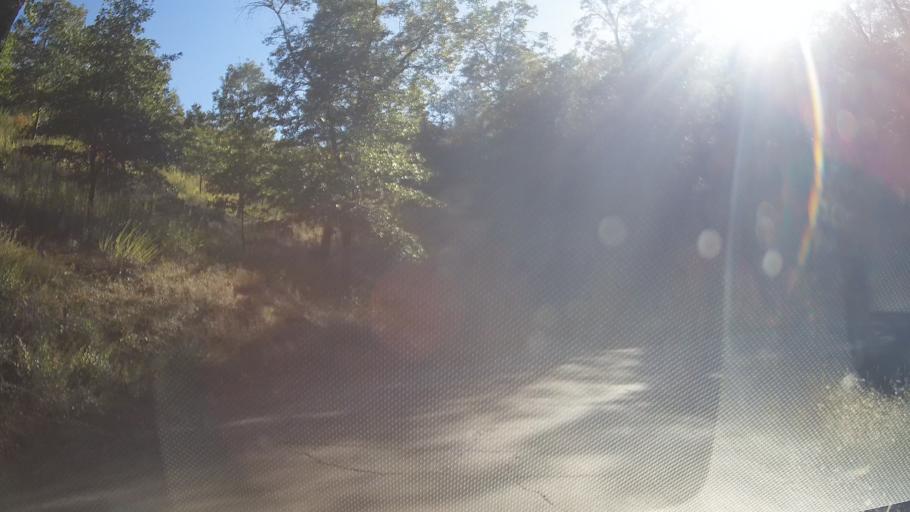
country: US
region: California
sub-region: San Diego County
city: Julian
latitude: 33.0543
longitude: -116.6272
